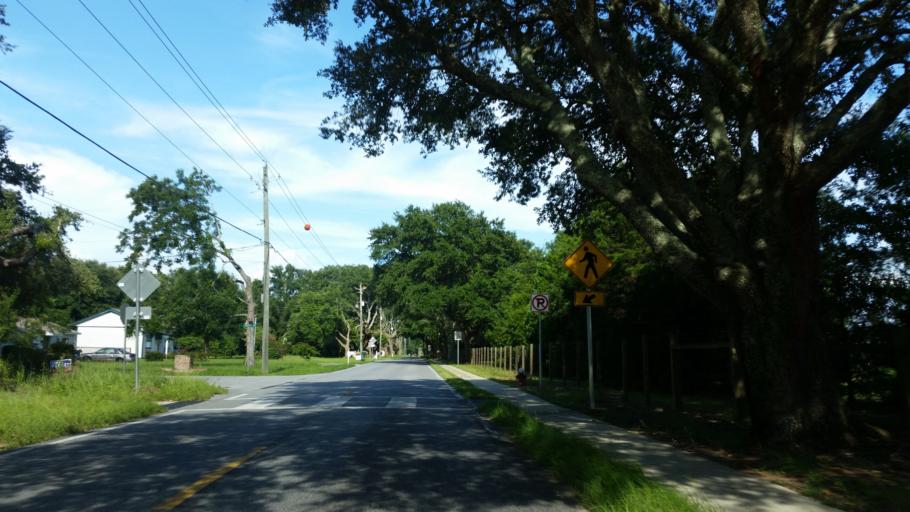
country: US
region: Florida
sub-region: Santa Rosa County
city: Pace
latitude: 30.6324
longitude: -87.1407
